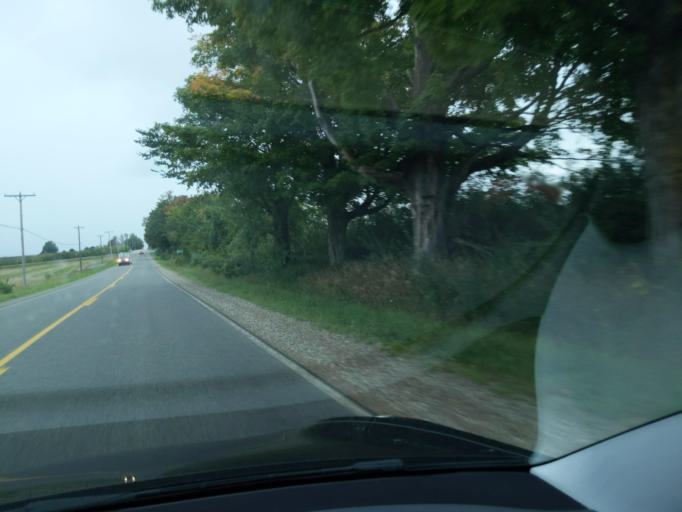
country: US
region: Michigan
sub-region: Antrim County
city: Elk Rapids
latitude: 44.8282
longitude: -85.4051
